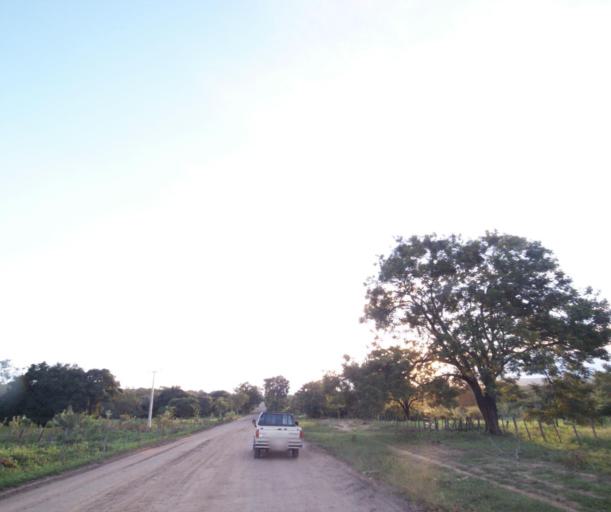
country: BR
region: Bahia
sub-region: Sao Felix Do Coribe
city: Santa Maria da Vitoria
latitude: -13.6267
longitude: -44.4220
